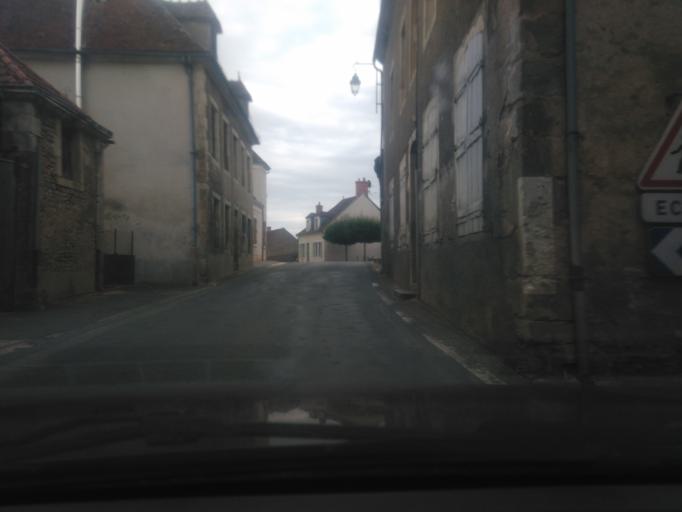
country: FR
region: Centre
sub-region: Departement du Cher
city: Charenton-du-Cher
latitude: 46.7294
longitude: 2.6432
